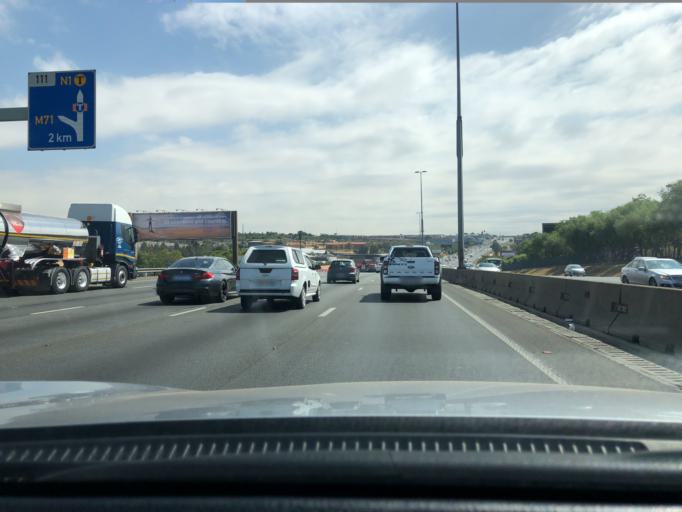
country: ZA
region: Gauteng
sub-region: City of Johannesburg Metropolitan Municipality
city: Midrand
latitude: -26.0004
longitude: 28.1211
